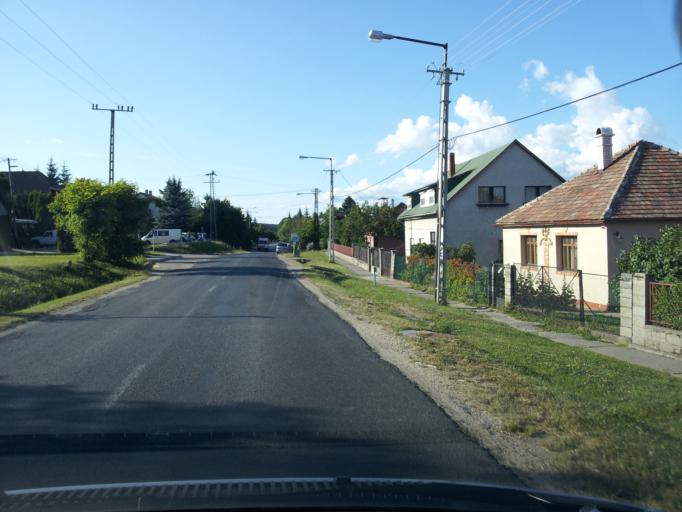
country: HU
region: Veszprem
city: Zirc
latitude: 47.2562
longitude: 17.8660
